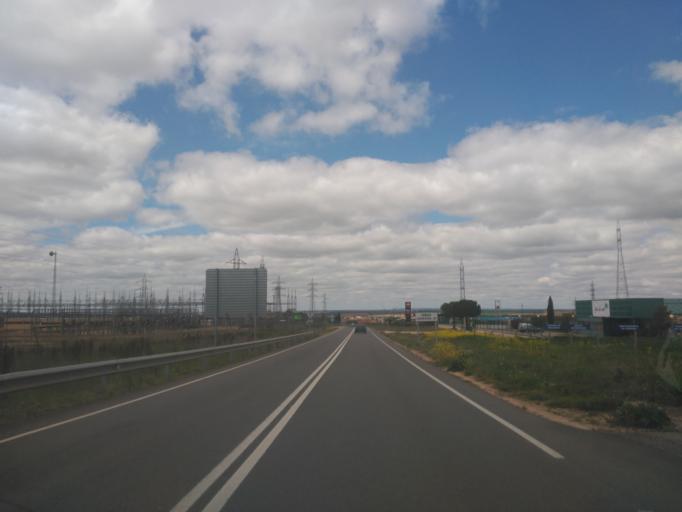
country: ES
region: Castille and Leon
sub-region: Provincia de Salamanca
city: Villamayor
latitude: 40.9878
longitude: -5.6861
